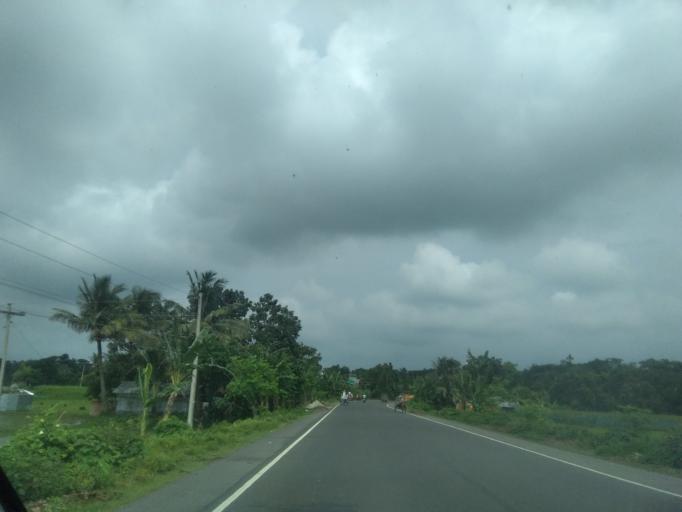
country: BD
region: Khulna
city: Kesabpur
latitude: 22.8372
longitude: 89.3036
